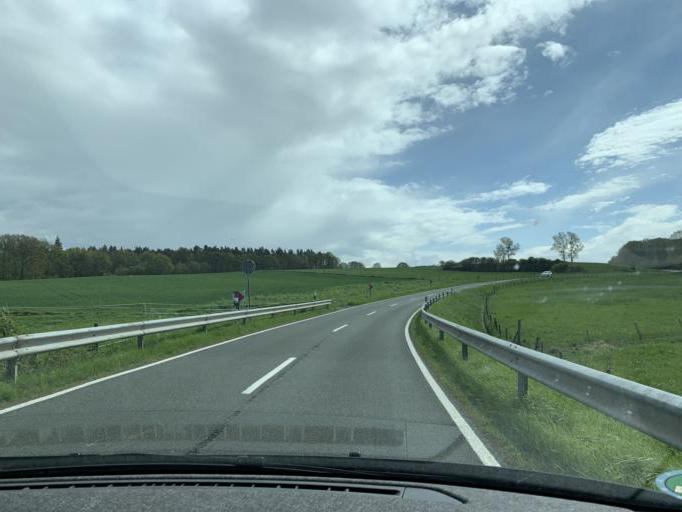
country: DE
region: North Rhine-Westphalia
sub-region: Regierungsbezirk Koln
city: Bad Munstereifel
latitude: 50.6054
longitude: 6.7221
